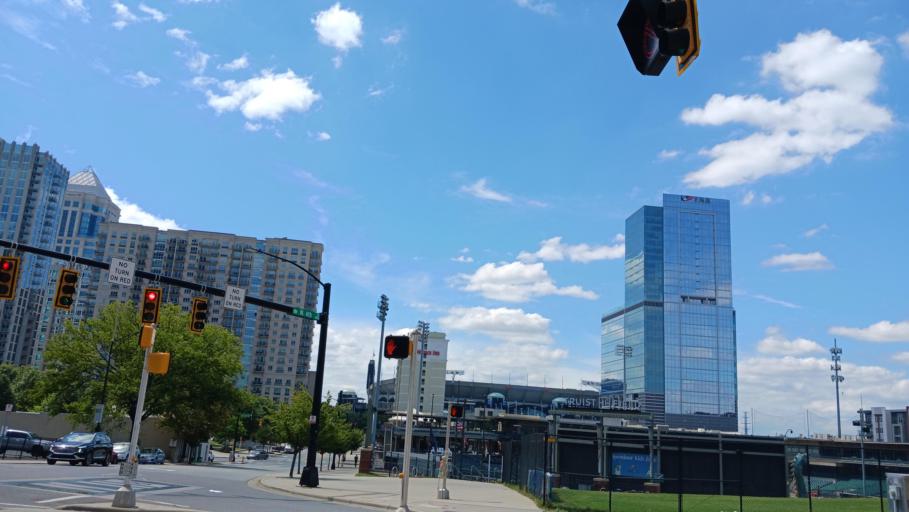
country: US
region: North Carolina
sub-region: Mecklenburg County
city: Charlotte
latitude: 35.2287
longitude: -80.8468
